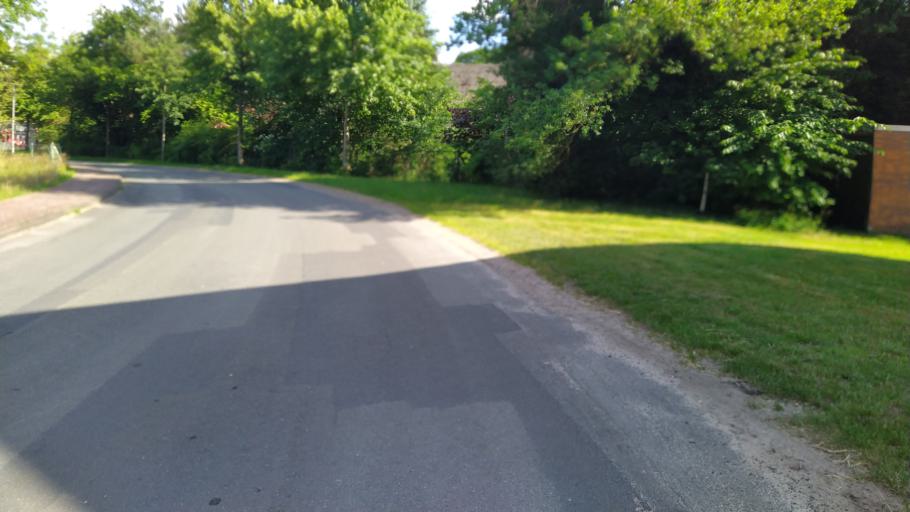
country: DE
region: Lower Saxony
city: Lintig
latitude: 53.6280
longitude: 8.8958
